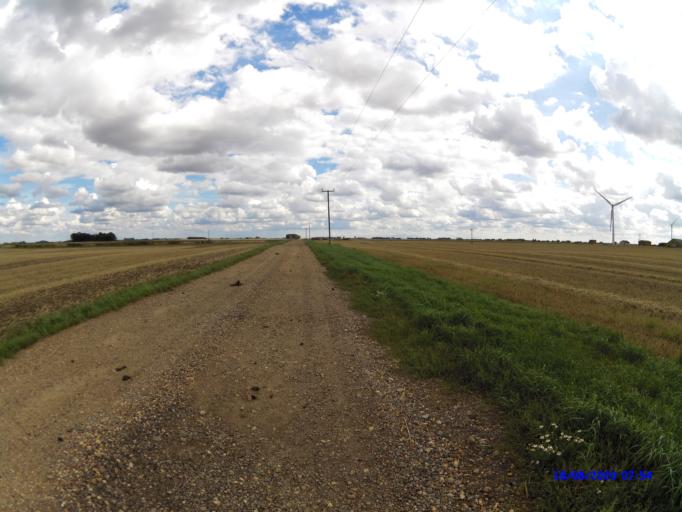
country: GB
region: England
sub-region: Cambridgeshire
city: Whittlesey
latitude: 52.5163
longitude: -0.0886
